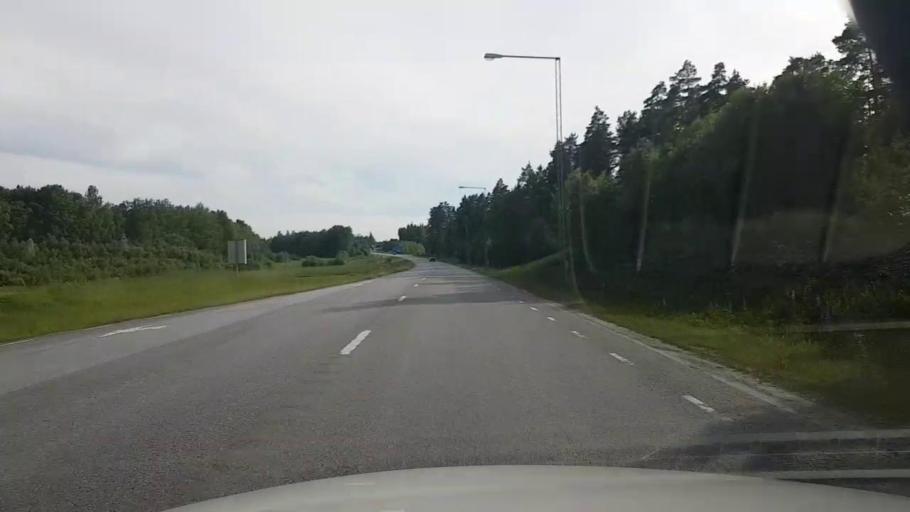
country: SE
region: Stockholm
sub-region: Sigtuna Kommun
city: Rosersberg
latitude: 59.6343
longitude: 17.9327
